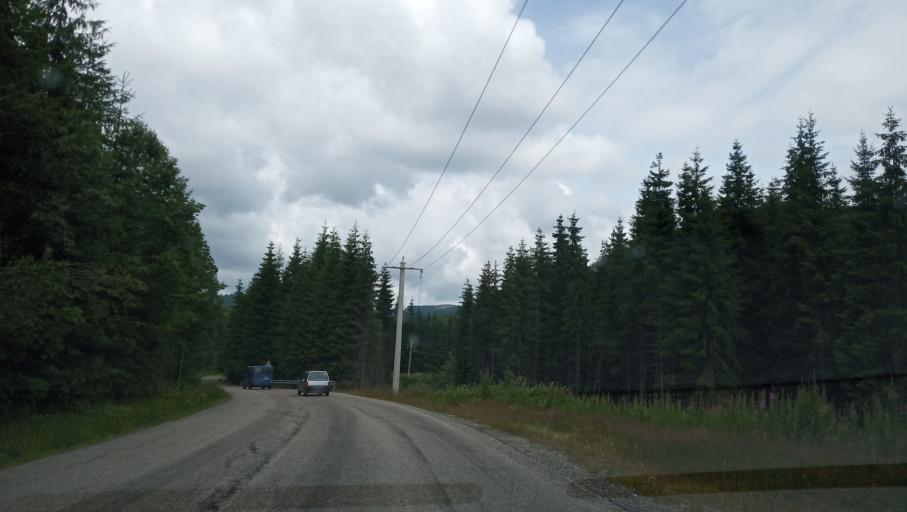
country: RO
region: Gorj
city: Novaci-Straini
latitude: 45.4311
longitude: 23.6703
